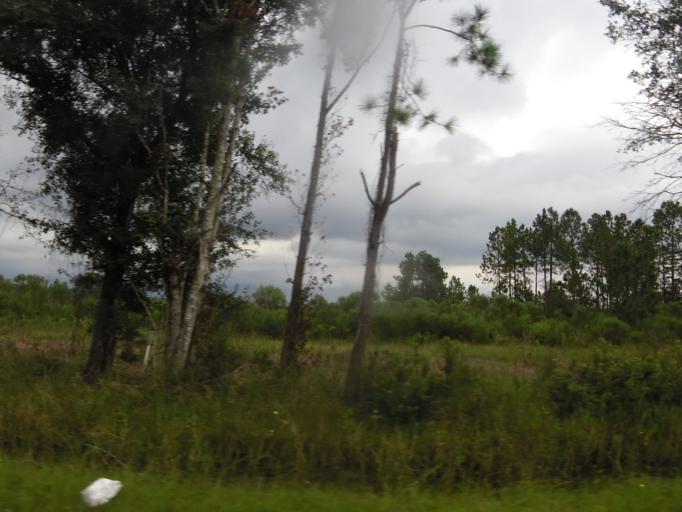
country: US
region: Florida
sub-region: Clay County
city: Middleburg
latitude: 30.1144
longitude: -81.8355
